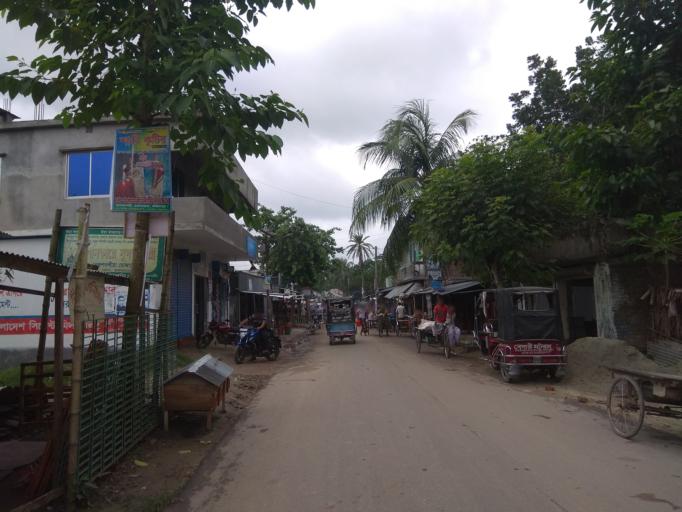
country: BD
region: Dhaka
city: Dohar
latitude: 23.4395
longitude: 90.0729
